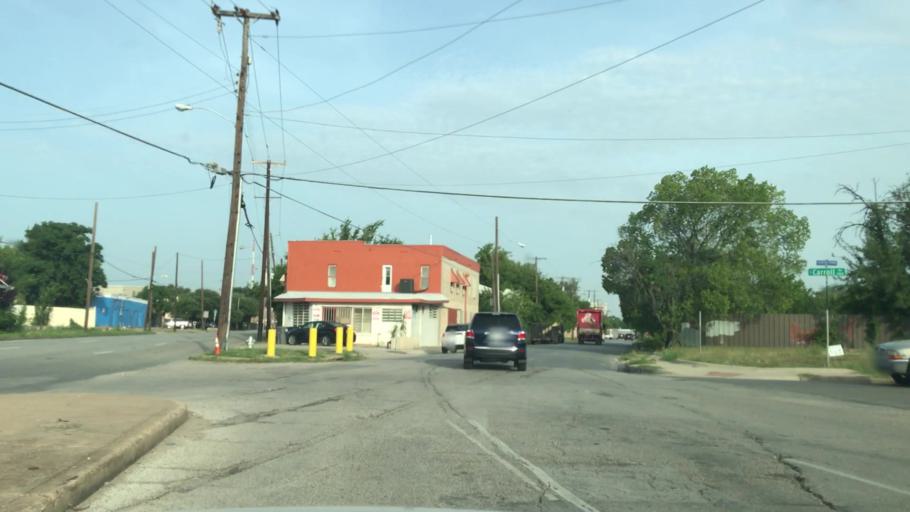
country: US
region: Texas
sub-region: Dallas County
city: Dallas
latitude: 32.7841
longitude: -96.7591
